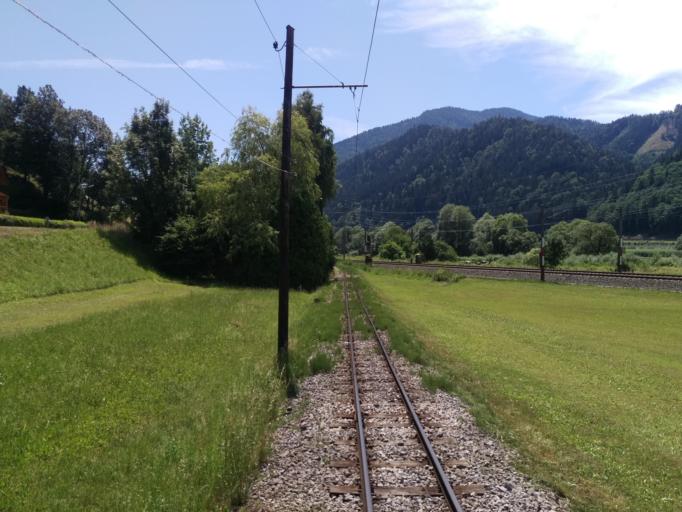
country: AT
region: Styria
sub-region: Politischer Bezirk Bruck-Muerzzuschlag
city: Pernegg an der Mur
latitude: 47.3414
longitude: 15.3553
